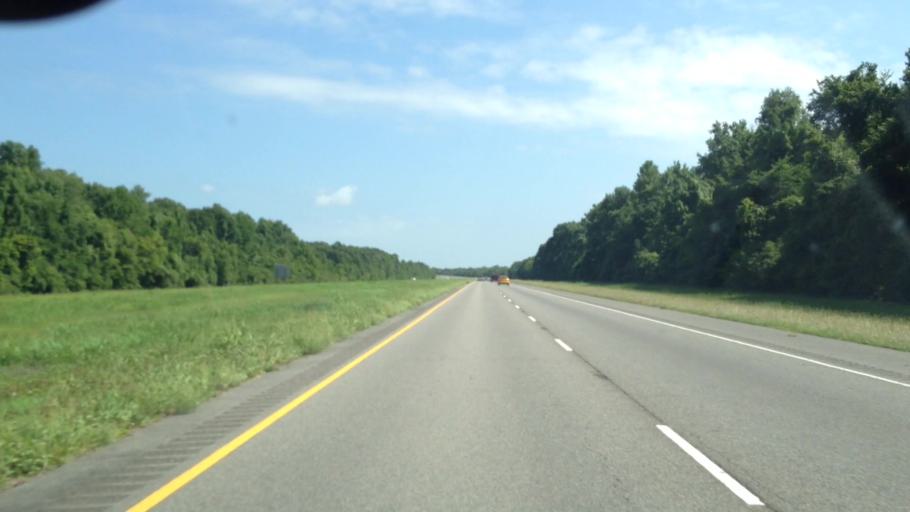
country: US
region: Louisiana
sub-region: Avoyelles Parish
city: Bunkie
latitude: 30.8836
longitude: -92.2270
